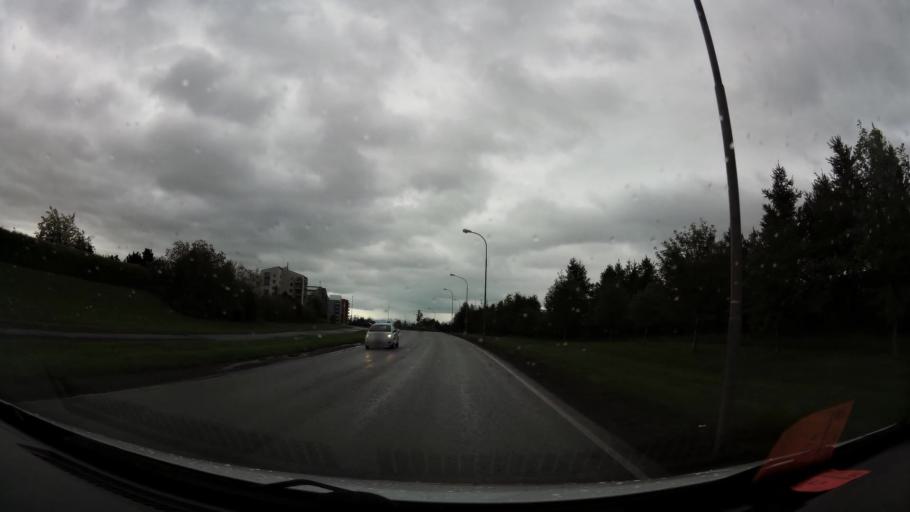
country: IS
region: Northeast
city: Akureyri
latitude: 65.6837
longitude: -18.1280
